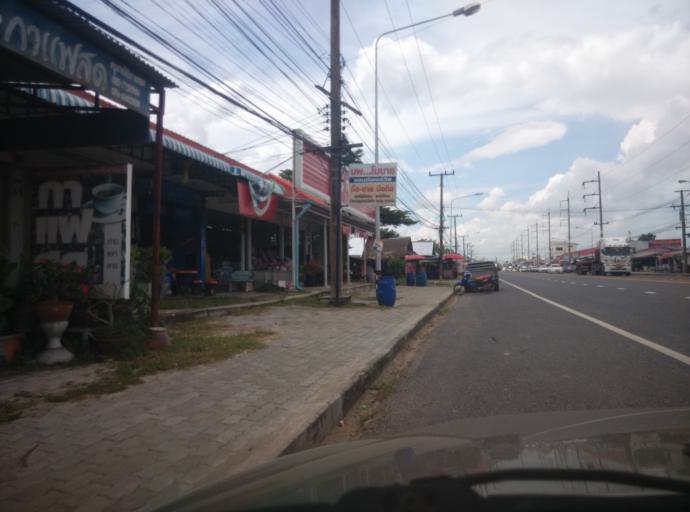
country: TH
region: Sisaket
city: Huai Thap Than
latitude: 15.0515
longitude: 104.0275
